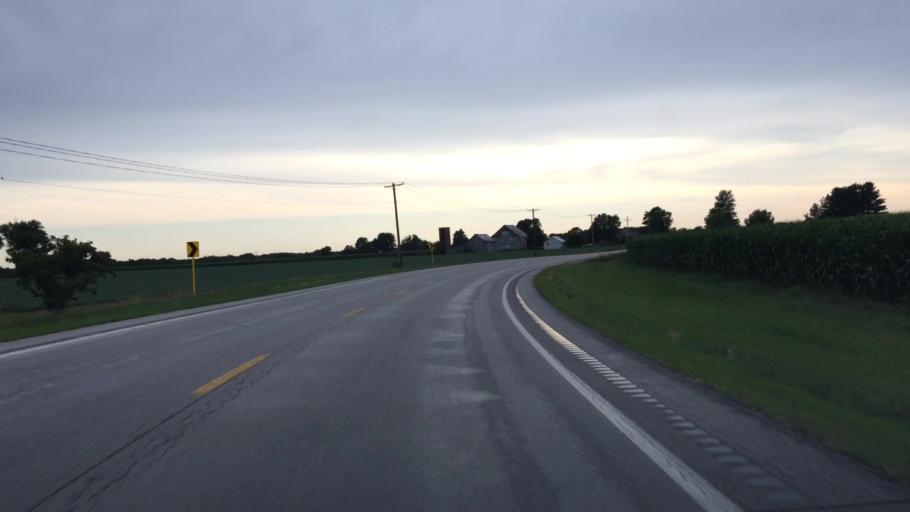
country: US
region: Illinois
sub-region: Hancock County
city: Hamilton
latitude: 40.3632
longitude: -91.3448
